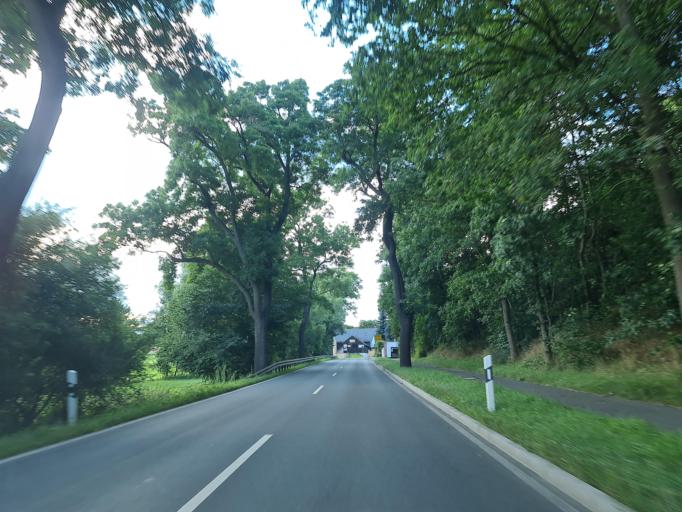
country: DE
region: Saxony
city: Pausa
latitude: 50.5741
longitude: 11.9940
